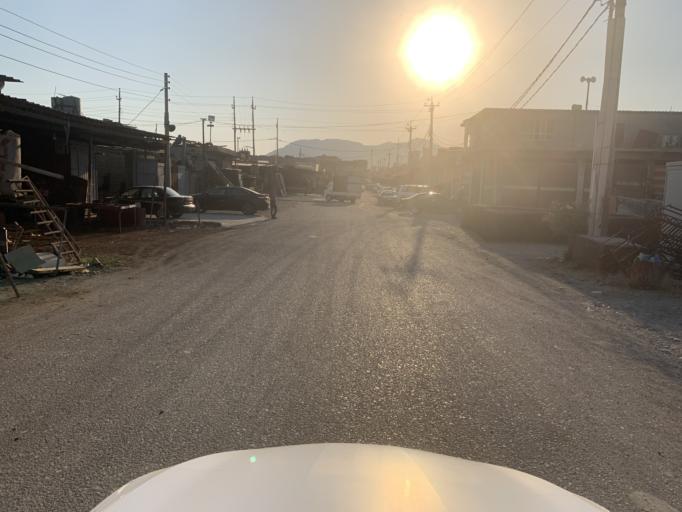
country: IQ
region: As Sulaymaniyah
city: Raniye
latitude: 36.2472
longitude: 44.8881
